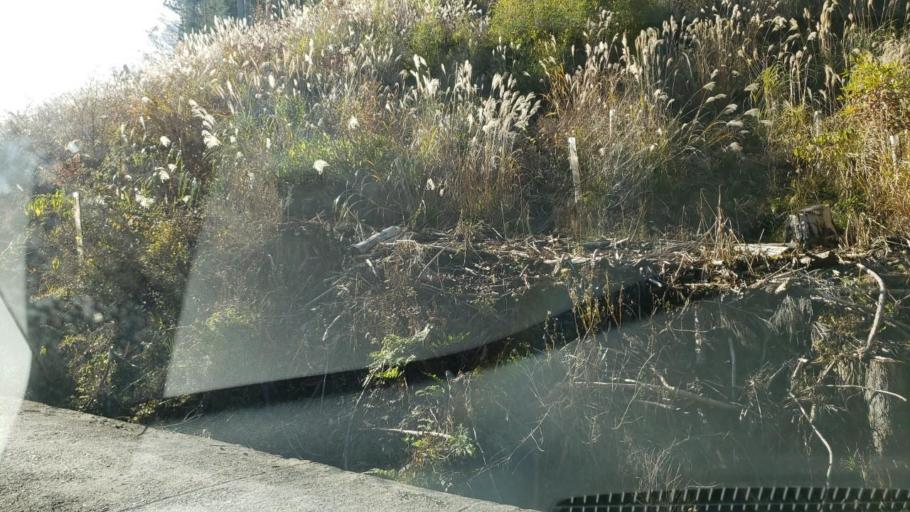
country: JP
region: Tokushima
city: Ikedacho
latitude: 33.9848
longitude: 133.9793
